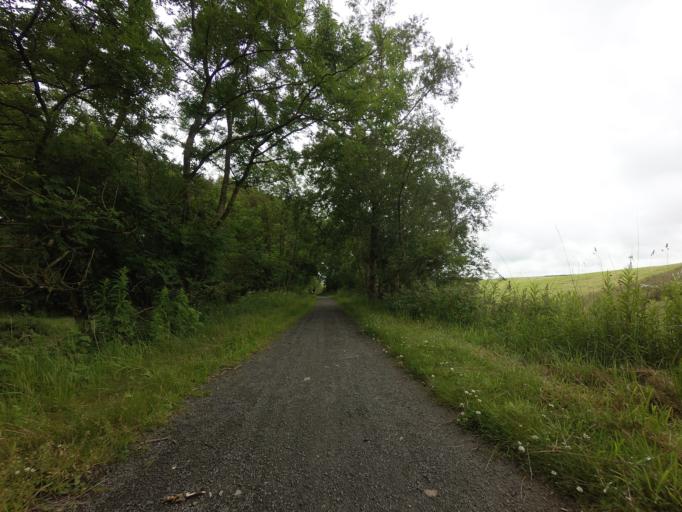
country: GB
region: Scotland
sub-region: Aberdeenshire
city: Mintlaw
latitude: 57.5116
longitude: -2.1408
